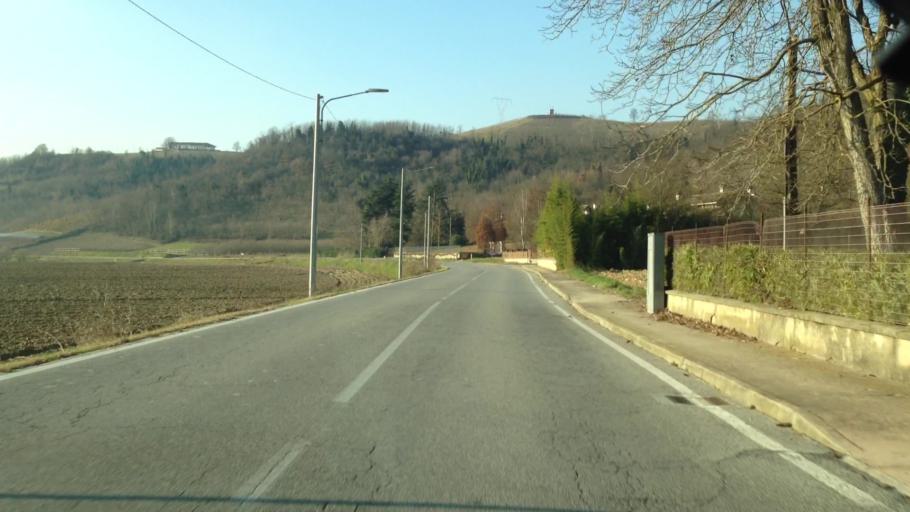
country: IT
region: Piedmont
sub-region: Provincia di Asti
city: Belveglio
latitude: 44.8297
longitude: 8.3242
